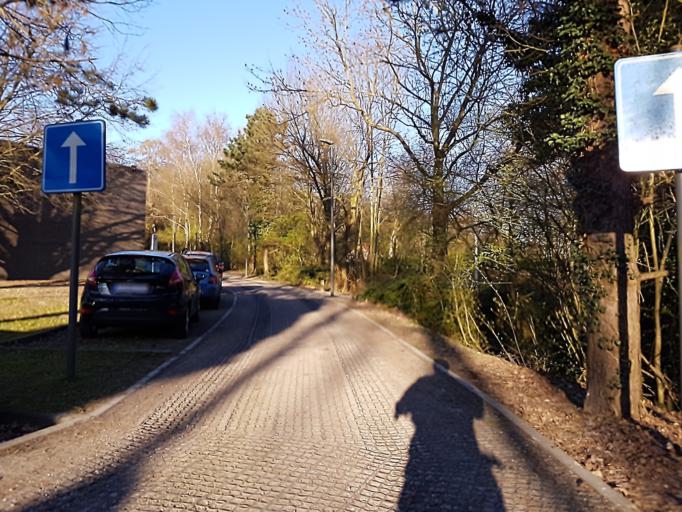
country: BE
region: Flanders
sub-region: Provincie Vlaams-Brabant
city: Wemmel
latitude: 50.8831
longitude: 4.3071
